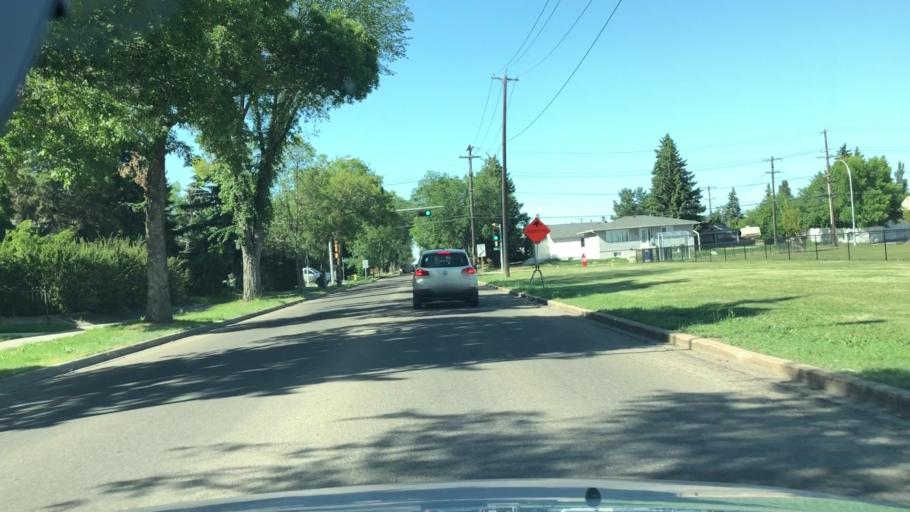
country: CA
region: Alberta
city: Edmonton
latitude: 53.5867
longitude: -113.5165
